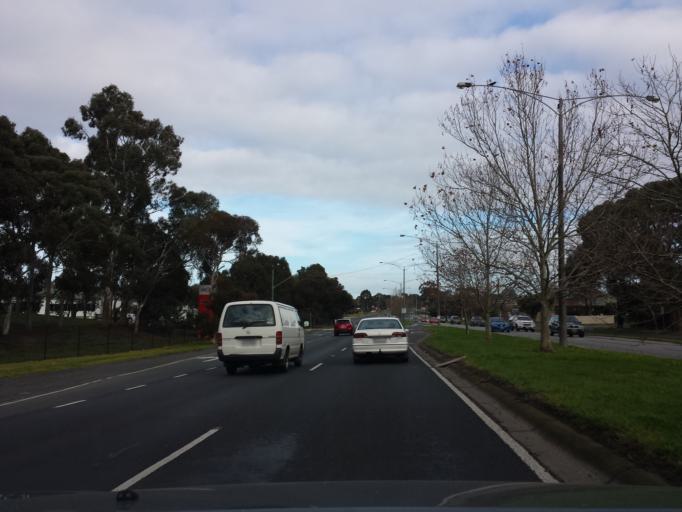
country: AU
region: Victoria
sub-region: Knox
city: Scoresby
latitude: -37.8984
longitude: 145.2379
